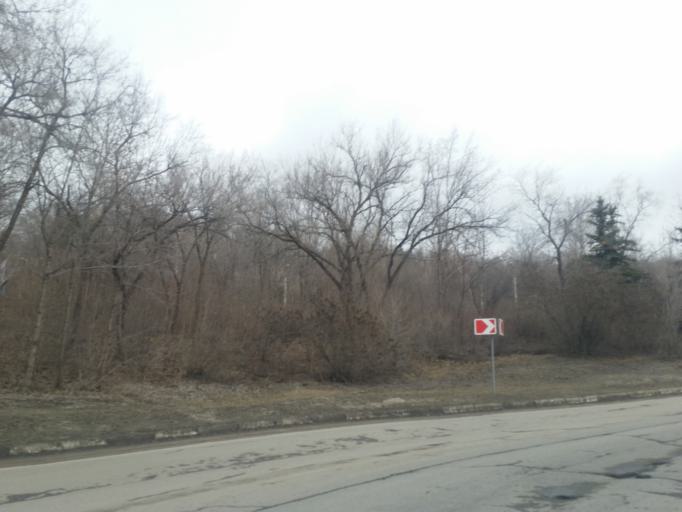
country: RU
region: Ulyanovsk
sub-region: Ulyanovskiy Rayon
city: Ulyanovsk
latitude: 54.3092
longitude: 48.4065
